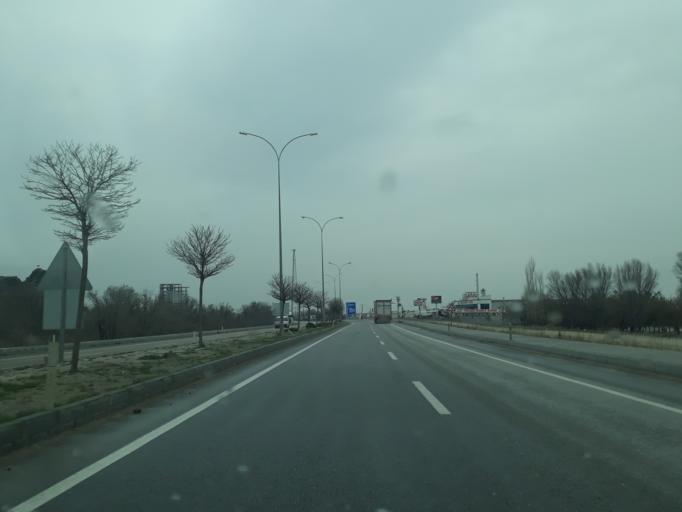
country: TR
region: Konya
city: Karapinar
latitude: 37.7152
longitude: 33.5791
